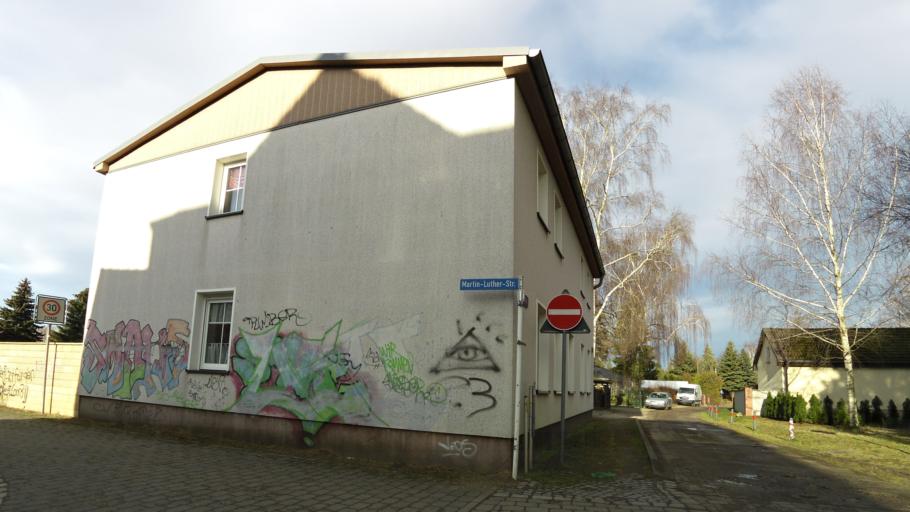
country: DE
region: Brandenburg
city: Petershagen
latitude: 52.5169
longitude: 13.7487
